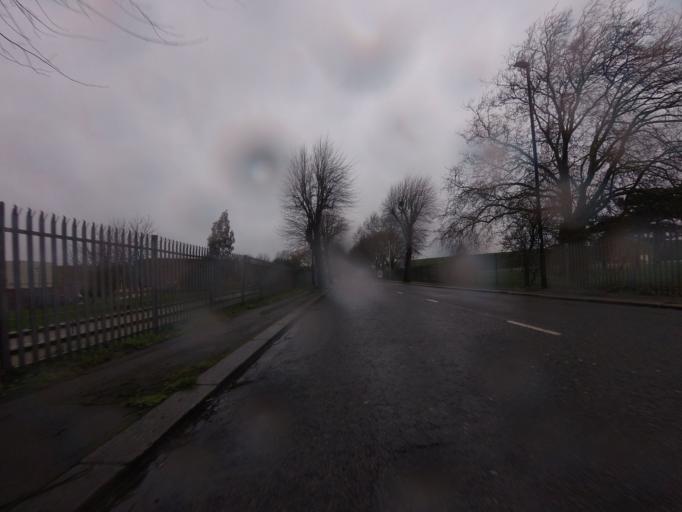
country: GB
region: England
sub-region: Greater London
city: Walthamstow
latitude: 51.6369
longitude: -0.0152
